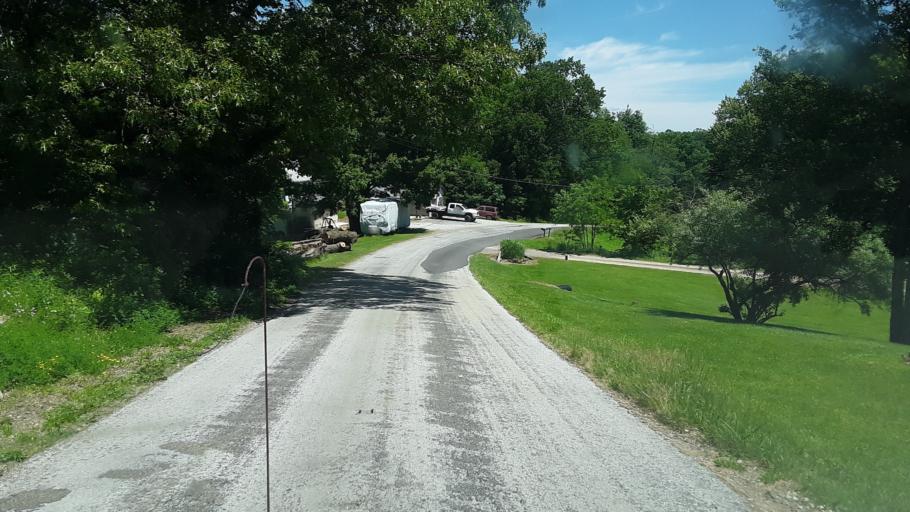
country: US
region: Ohio
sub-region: Coshocton County
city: Coshocton
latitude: 40.2688
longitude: -81.9247
